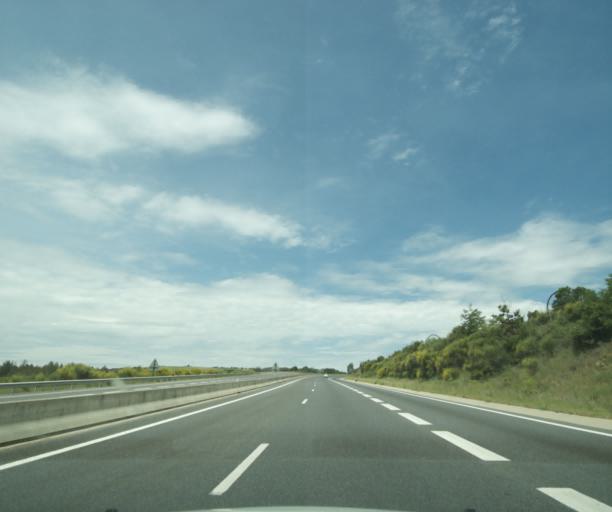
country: FR
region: Midi-Pyrenees
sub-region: Departement de l'Aveyron
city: Severac-le-Chateau
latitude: 44.2279
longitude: 3.0682
